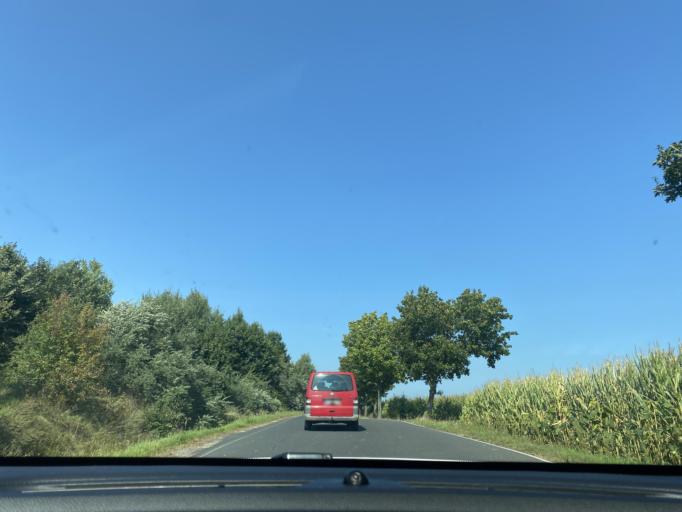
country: DE
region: Saxony
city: Quitzdorf
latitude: 51.2284
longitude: 14.7744
